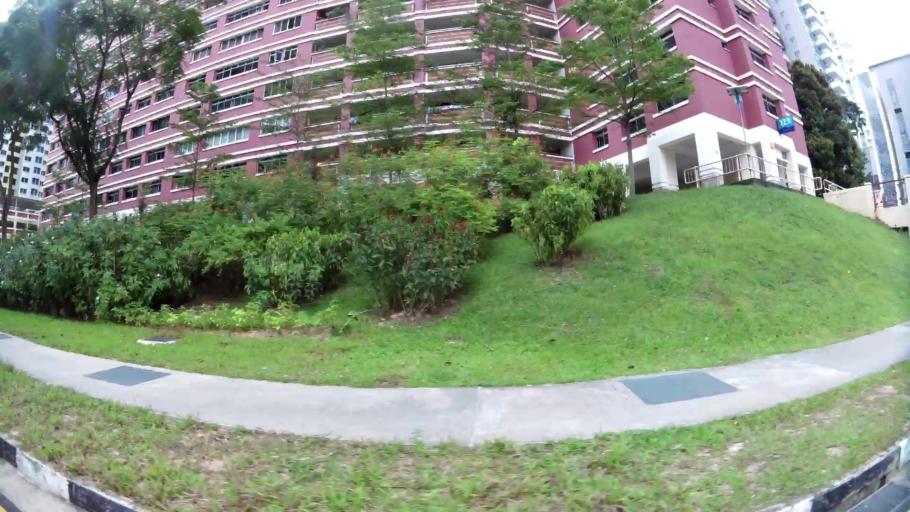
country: SG
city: Singapore
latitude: 1.2835
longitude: 103.8293
